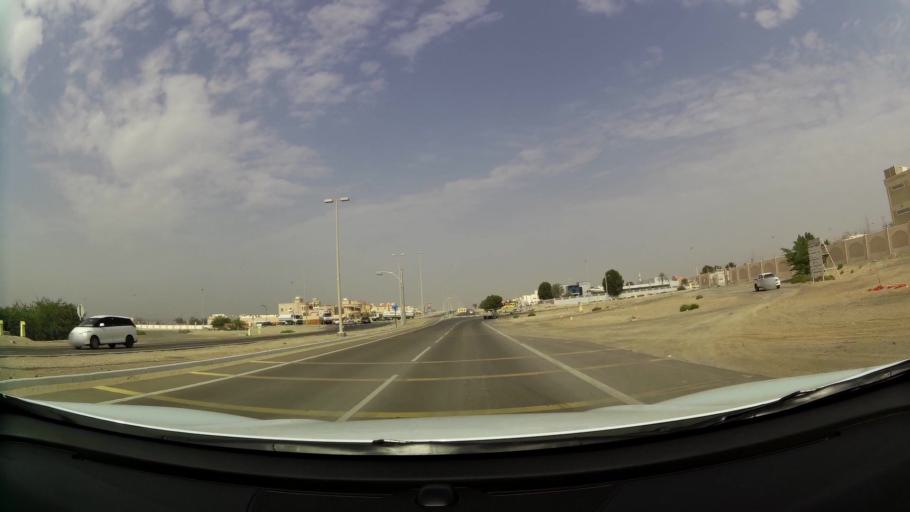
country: AE
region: Abu Dhabi
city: Abu Dhabi
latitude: 24.2916
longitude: 54.6591
